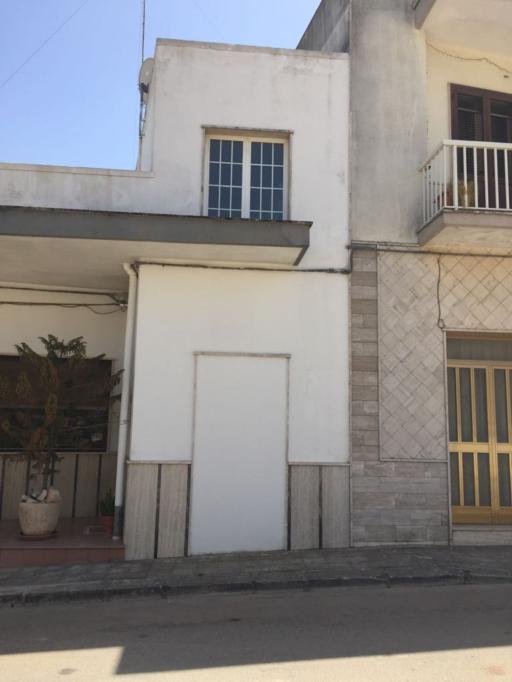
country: IT
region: Apulia
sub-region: Provincia di Brindisi
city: Casalini
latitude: 40.7366
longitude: 17.4741
